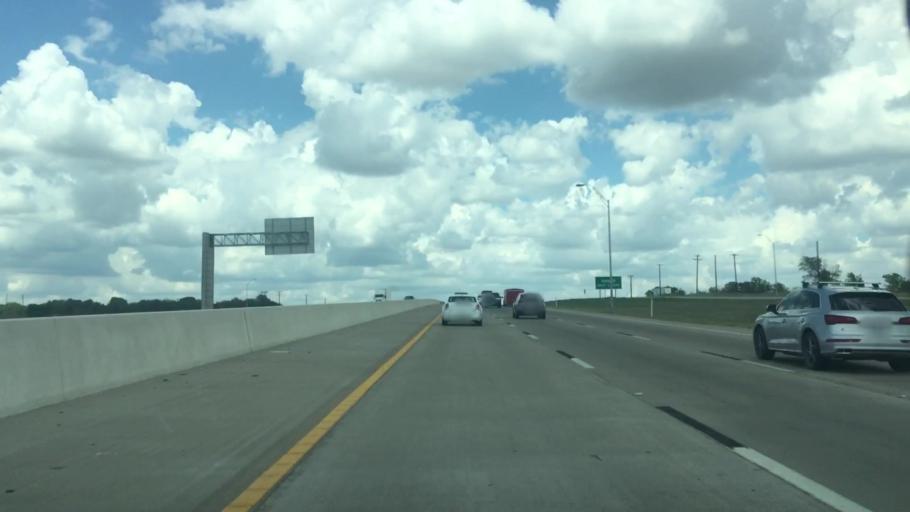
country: US
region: Texas
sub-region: McLennan County
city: Lorena
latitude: 31.3965
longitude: -97.2080
